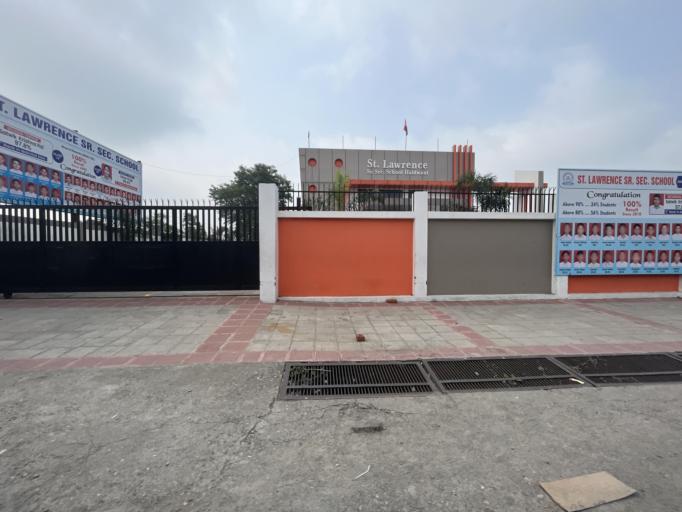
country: IN
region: Uttarakhand
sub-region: Naini Tal
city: Haldwani
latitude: 29.1943
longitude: 79.5032
